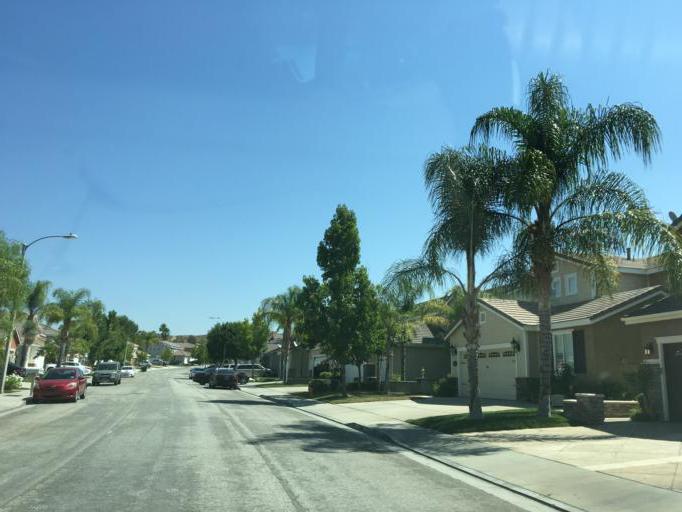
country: US
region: California
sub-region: Los Angeles County
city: Santa Clarita
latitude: 34.3928
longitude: -118.5881
